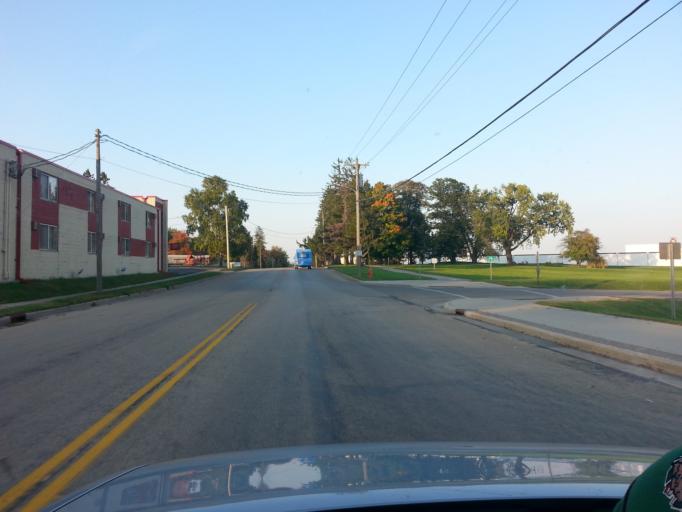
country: US
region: Minnesota
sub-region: Olmsted County
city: Rochester
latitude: 43.9894
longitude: -92.4612
